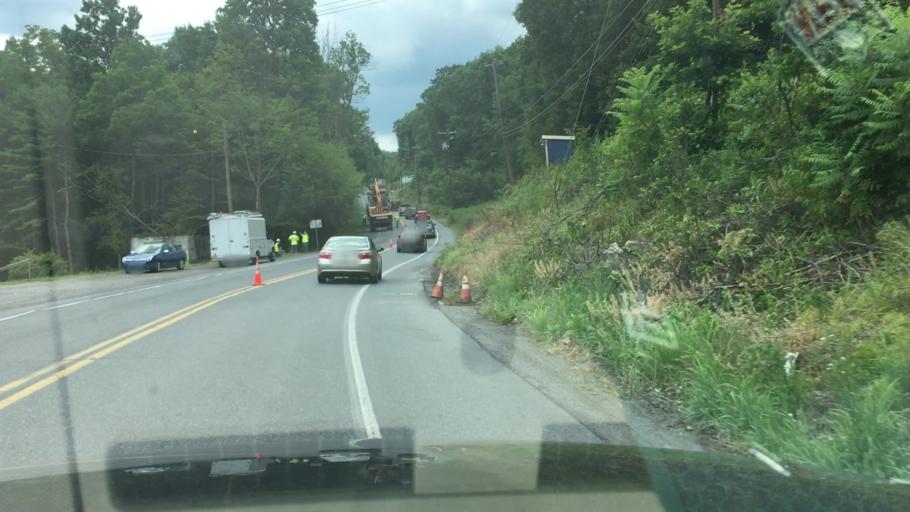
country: US
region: Pennsylvania
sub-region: Schuylkill County
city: Minersville
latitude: 40.7003
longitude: -76.2893
